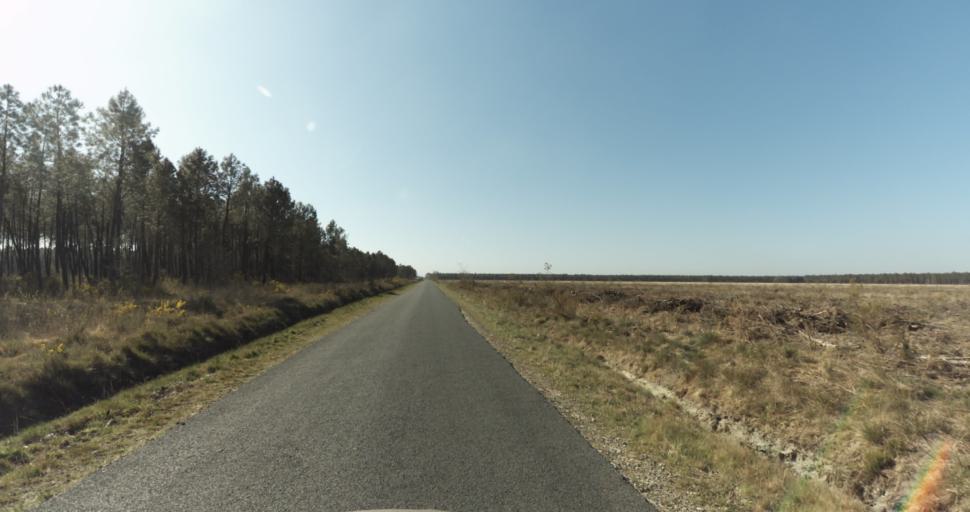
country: FR
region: Aquitaine
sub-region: Departement de la Gironde
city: Marcheprime
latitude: 44.7832
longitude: -0.8615
